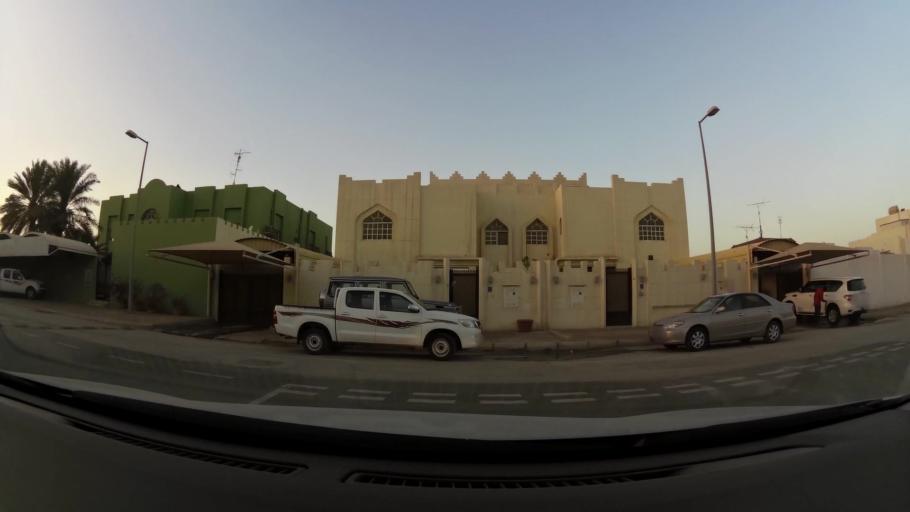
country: QA
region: Baladiyat ar Rayyan
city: Ar Rayyan
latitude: 25.3255
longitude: 51.4623
